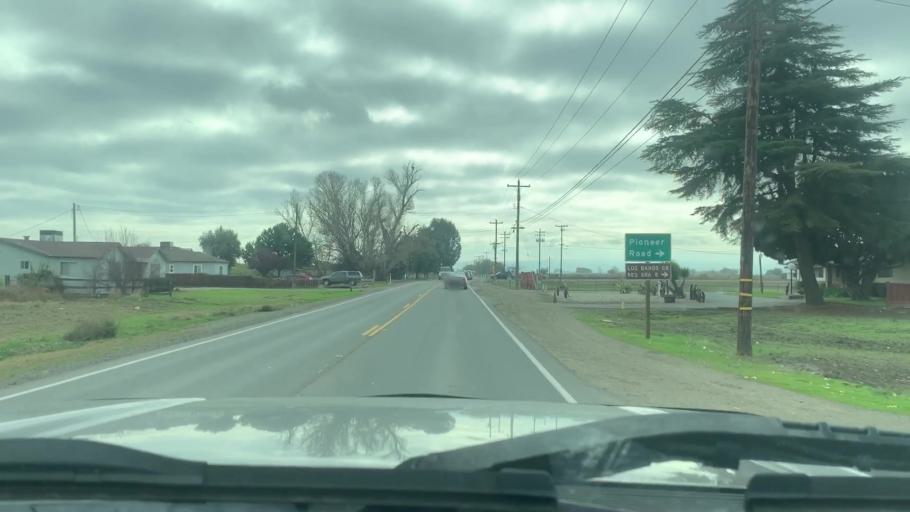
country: US
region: California
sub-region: Merced County
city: Los Banos
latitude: 37.0438
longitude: -120.8357
